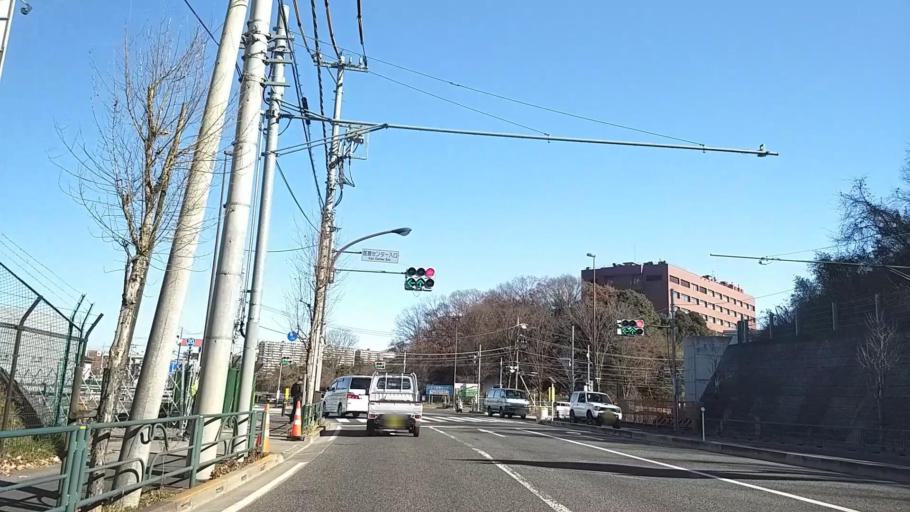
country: JP
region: Tokyo
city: Hachioji
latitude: 35.6310
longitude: 139.2858
